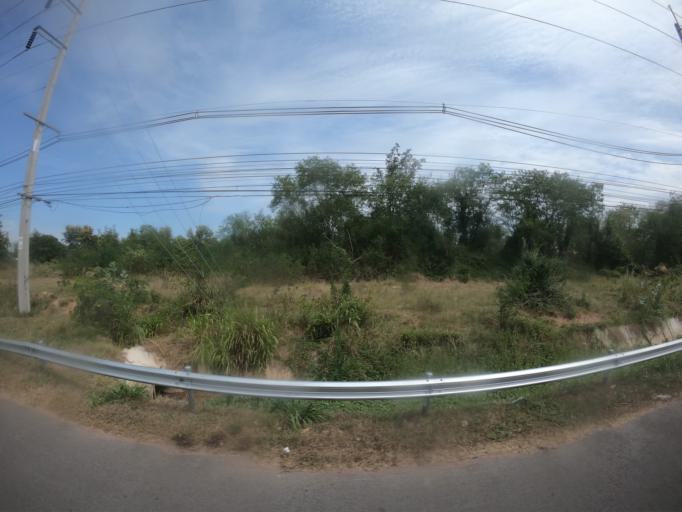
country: TH
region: Maha Sarakham
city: Chiang Yuen
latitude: 16.4164
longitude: 103.0819
